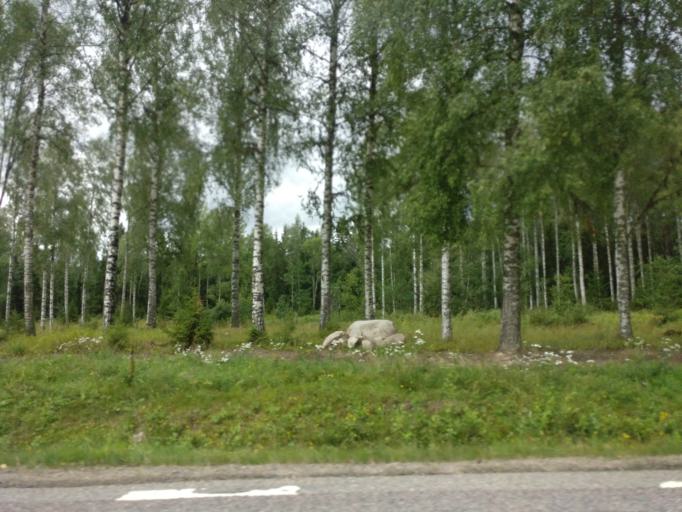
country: SE
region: Vaermland
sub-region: Torsby Kommun
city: Torsby
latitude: 60.7689
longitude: 12.7572
